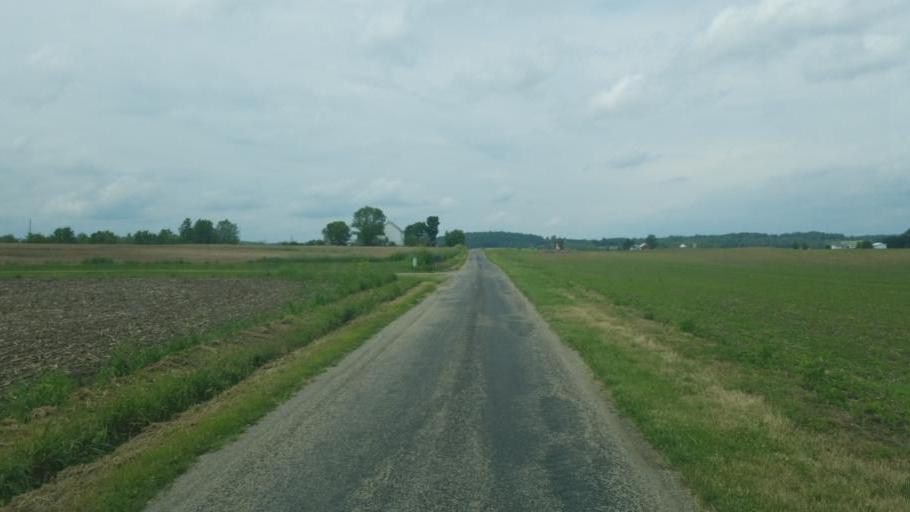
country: US
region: Ohio
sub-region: Perry County
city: Thornport
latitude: 39.9127
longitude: -82.3704
